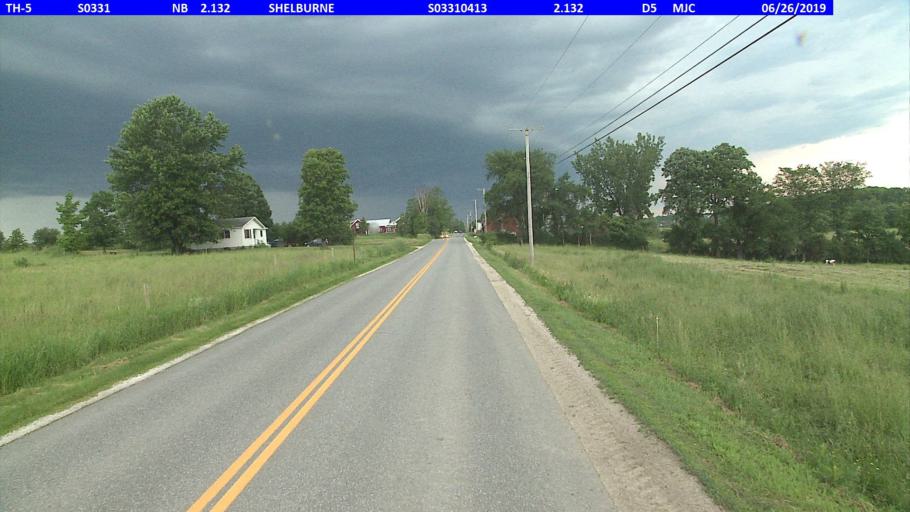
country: US
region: Vermont
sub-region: Chittenden County
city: South Burlington
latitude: 44.4011
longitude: -73.1781
